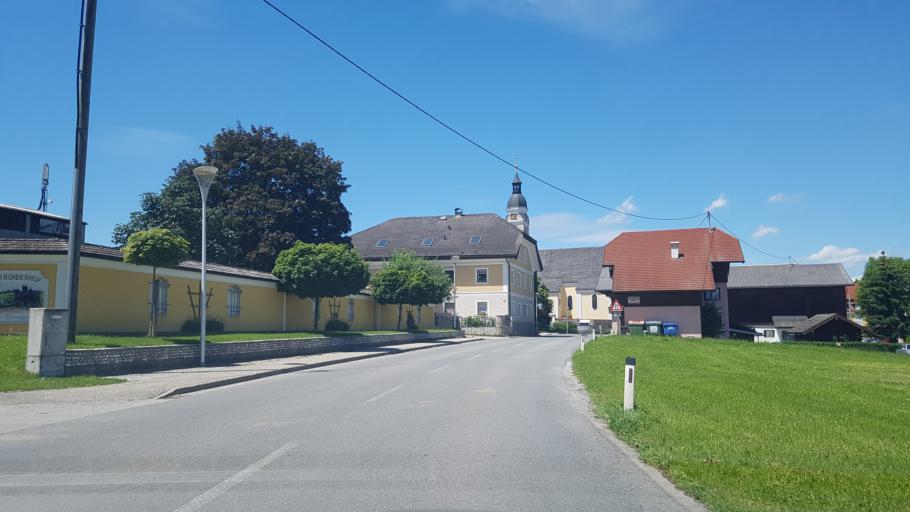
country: AT
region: Salzburg
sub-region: Politischer Bezirk Salzburg-Umgebung
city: Strasswalchen
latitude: 48.0038
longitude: 13.2193
